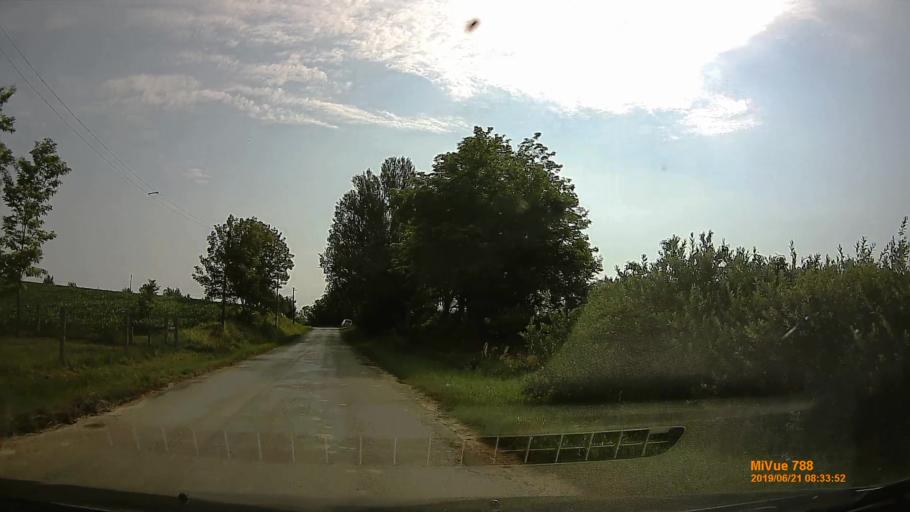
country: HU
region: Baranya
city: Buekkoesd
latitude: 46.1638
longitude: 17.8844
